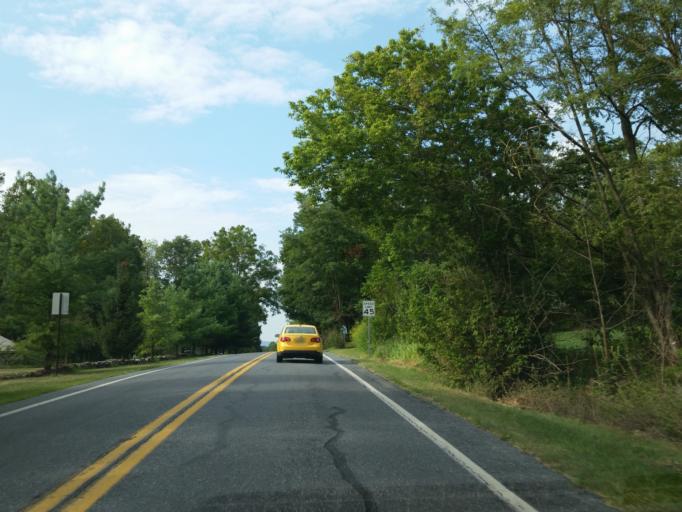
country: US
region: Pennsylvania
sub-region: Lebanon County
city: Annville
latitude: 40.3630
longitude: -76.5273
